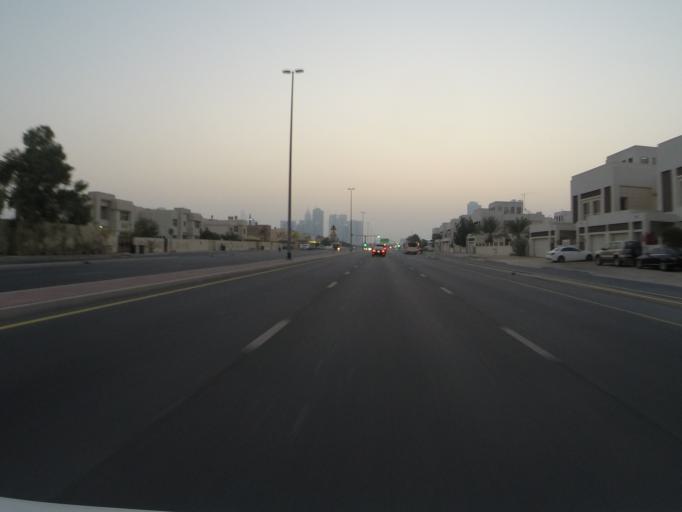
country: AE
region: Dubai
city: Dubai
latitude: 25.1057
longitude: 55.1965
